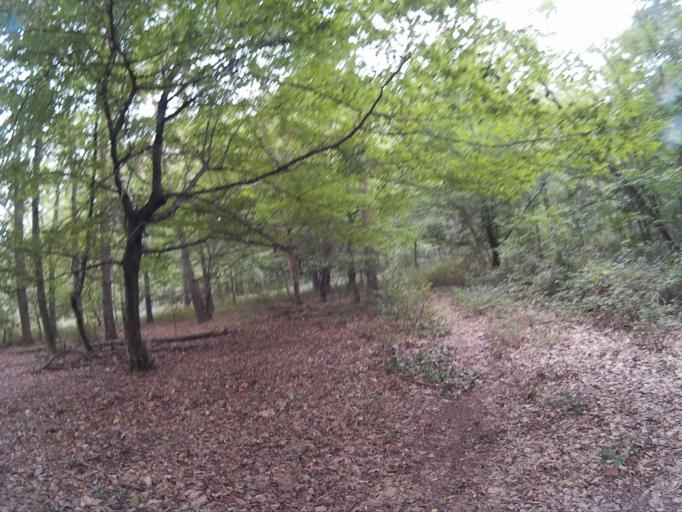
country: HU
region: Zala
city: Zalalovo
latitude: 46.7900
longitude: 16.5161
